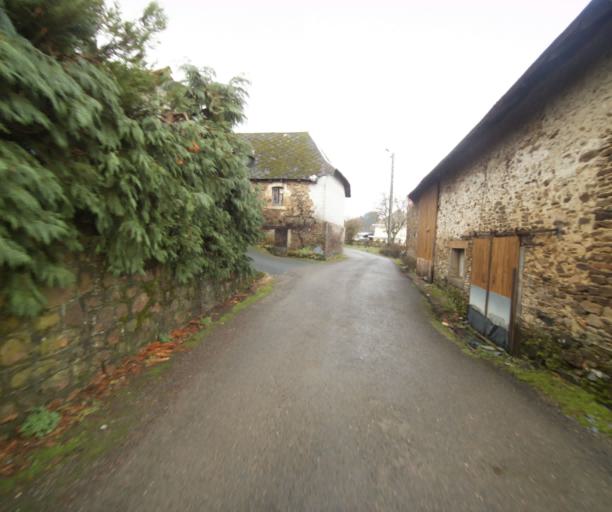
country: FR
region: Limousin
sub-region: Departement de la Correze
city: Cornil
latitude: 45.1909
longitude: 1.6461
